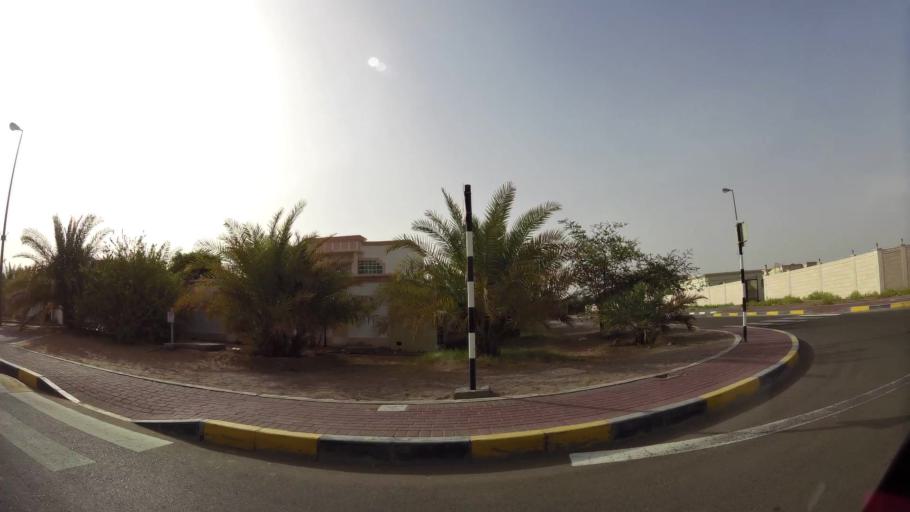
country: AE
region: Abu Dhabi
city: Al Ain
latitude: 24.2103
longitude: 55.6405
